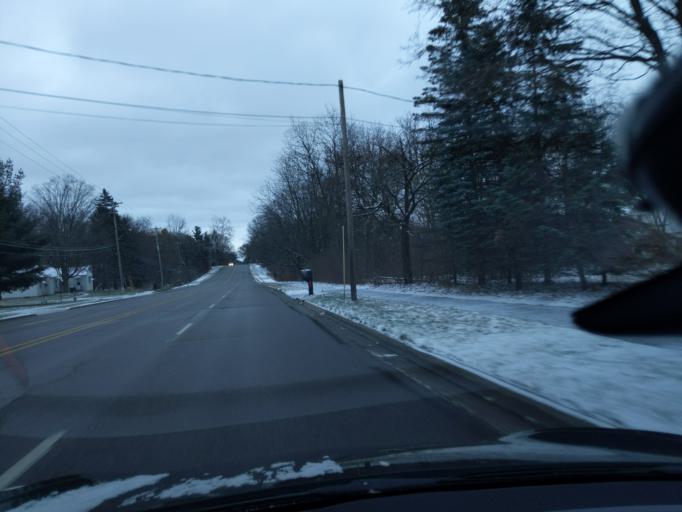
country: US
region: Michigan
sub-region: Ingham County
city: Okemos
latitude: 42.7118
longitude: -84.4579
